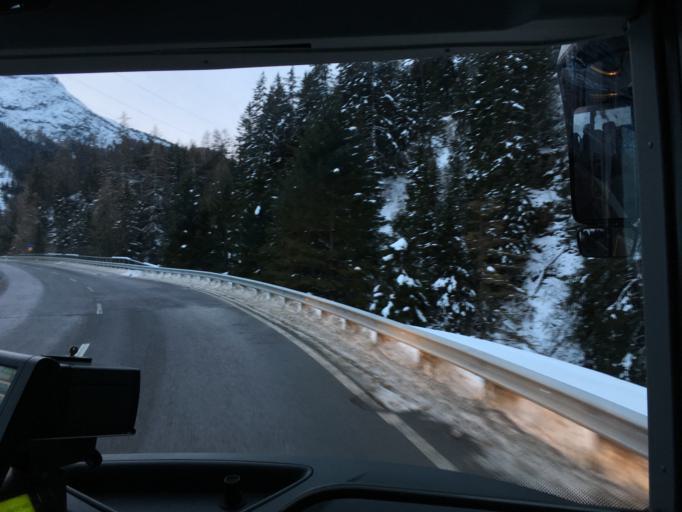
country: CH
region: Grisons
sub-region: Albula District
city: Tiefencastel
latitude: 46.5635
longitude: 9.6213
